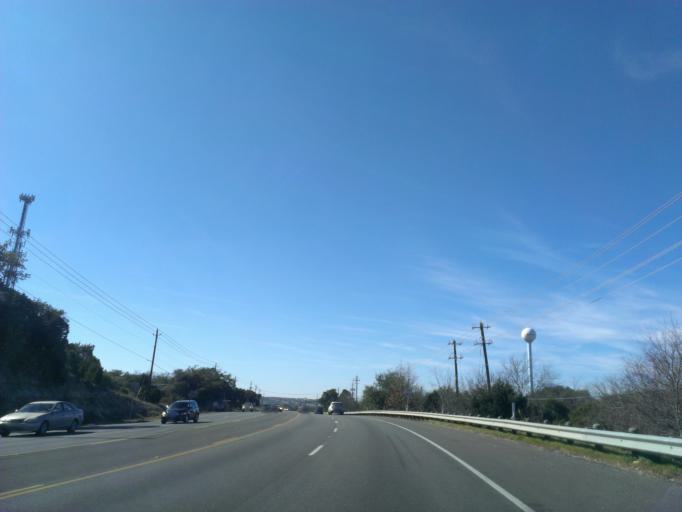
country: US
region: Texas
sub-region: Travis County
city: Lakeway
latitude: 30.3577
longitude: -97.9581
